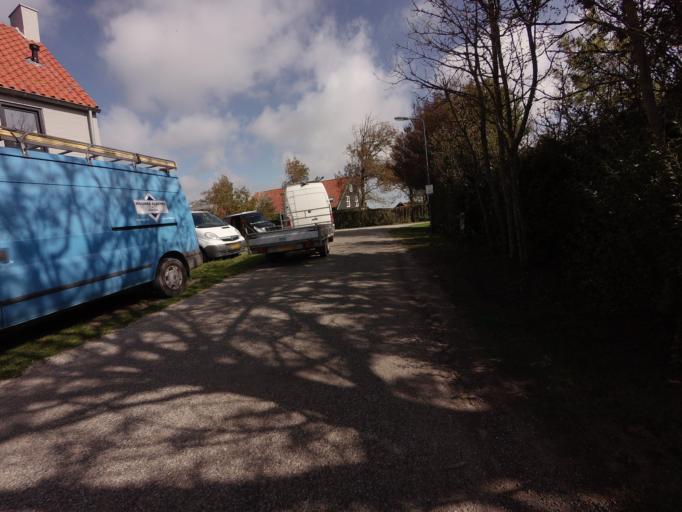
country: NL
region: Zeeland
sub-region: Gemeente Middelburg
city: Middelburg
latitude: 51.5227
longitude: 3.5281
